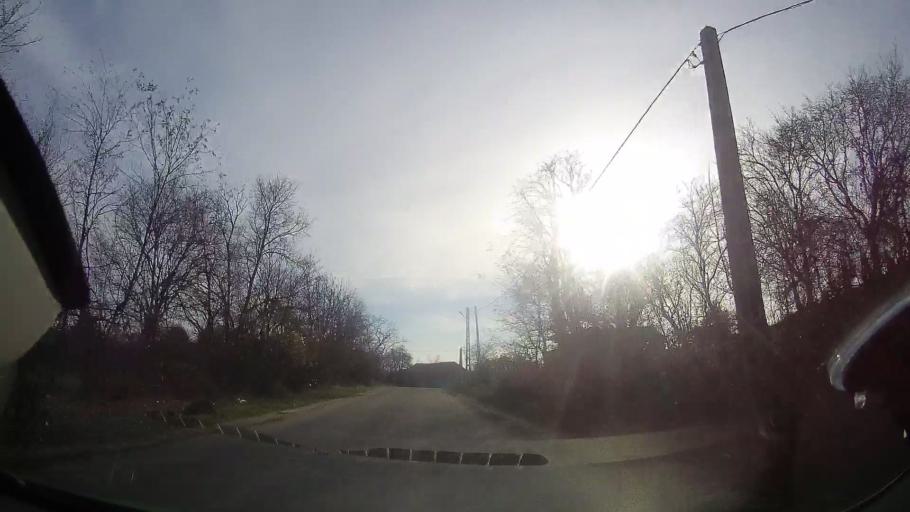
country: RO
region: Bihor
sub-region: Comuna Sarbi
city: Burzuc
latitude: 47.1241
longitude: 22.1857
